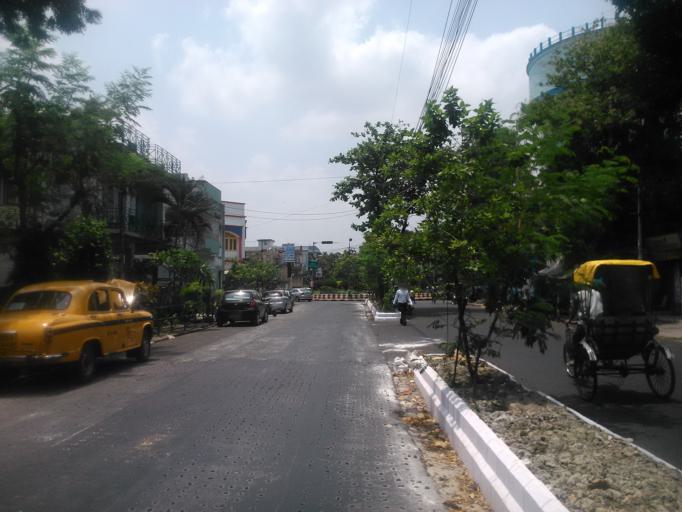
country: IN
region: West Bengal
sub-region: North 24 Parganas
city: Garui
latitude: 22.5966
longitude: 88.4098
